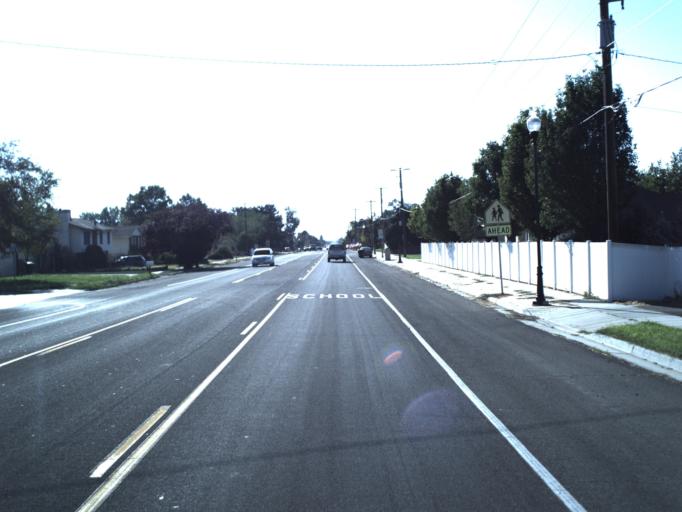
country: US
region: Utah
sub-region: Davis County
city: West Point
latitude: 41.1399
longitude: -112.0769
